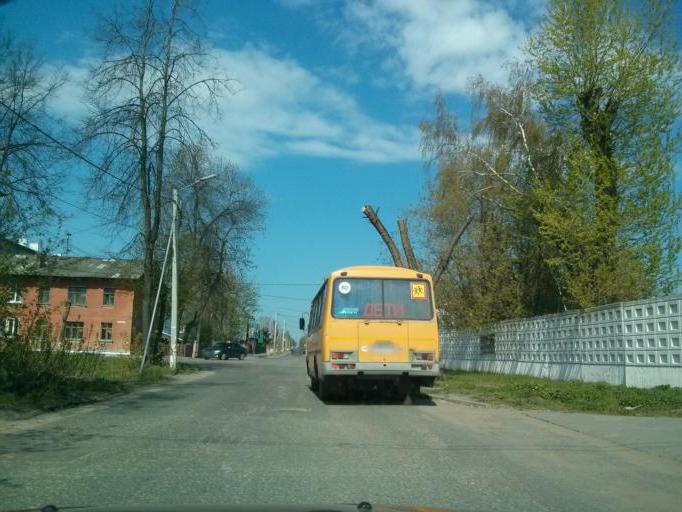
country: RU
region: Vladimir
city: Murom
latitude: 55.5660
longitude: 42.0668
